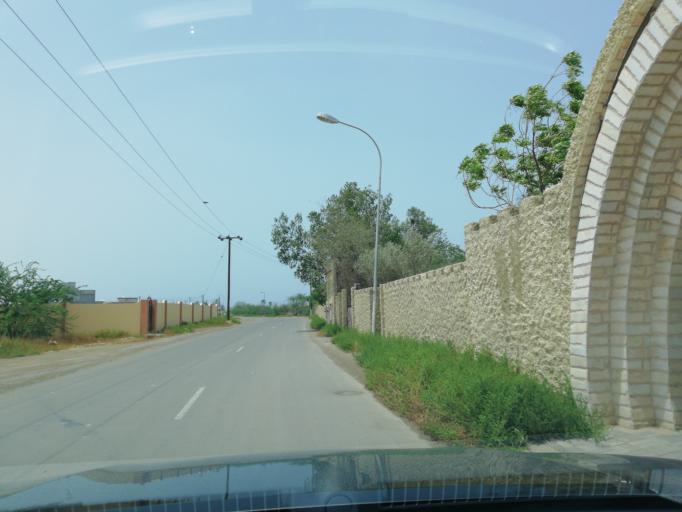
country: OM
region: Al Batinah
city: Al Liwa'
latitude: 24.6086
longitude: 56.5382
